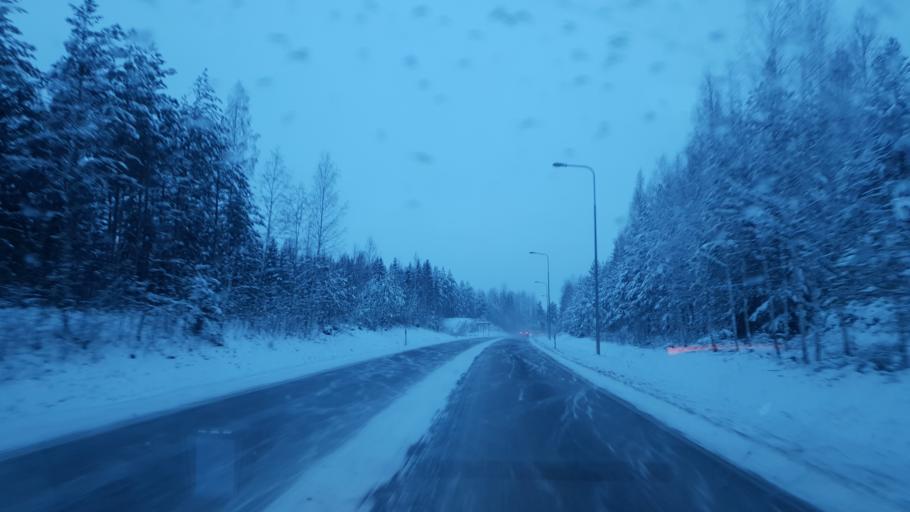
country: FI
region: Uusimaa
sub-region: Helsinki
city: Kerava
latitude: 60.3837
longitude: 25.1573
